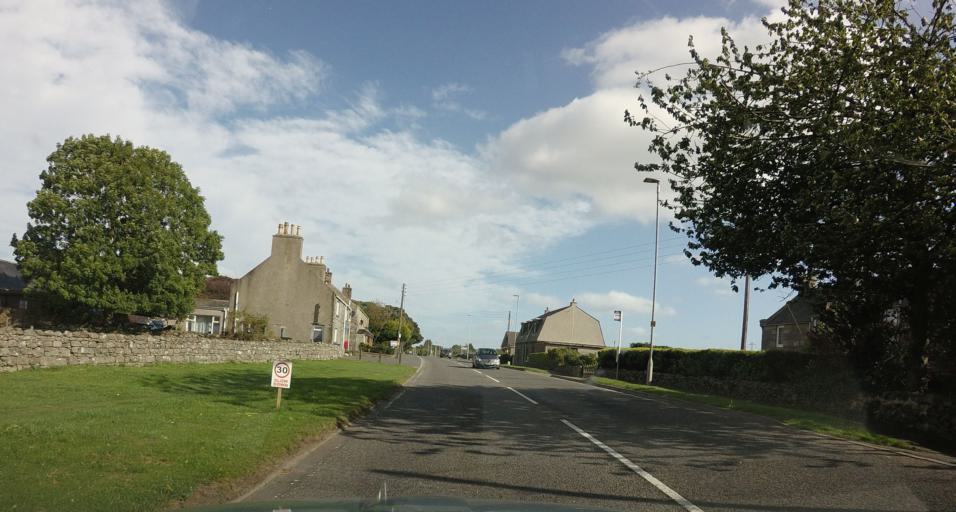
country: GB
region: Scotland
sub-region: Aberdeenshire
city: Westhill
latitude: 57.1523
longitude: -2.3158
